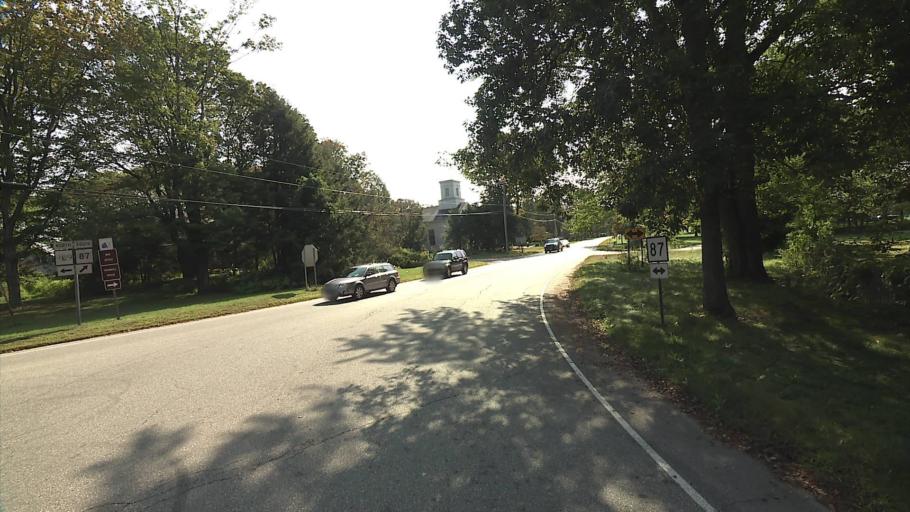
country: US
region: Connecticut
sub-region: Windham County
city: South Windham
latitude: 41.6463
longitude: -72.2240
